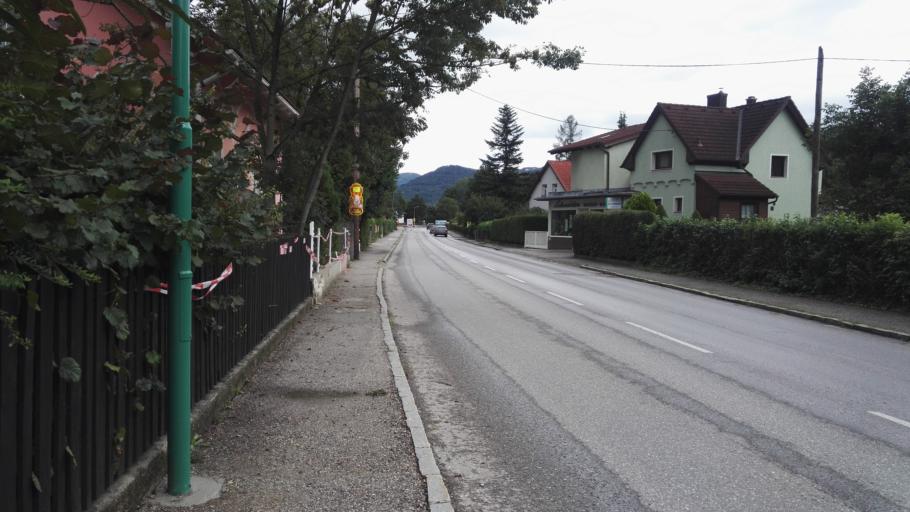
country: AT
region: Lower Austria
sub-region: Politischer Bezirk Neunkirchen
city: Payerbach
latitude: 47.6929
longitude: 15.8710
